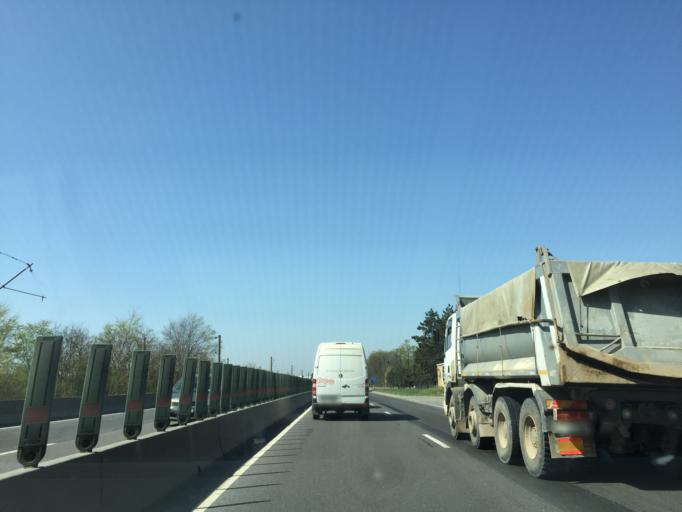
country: RO
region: Ilfov
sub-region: Comuna Otopeni
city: Otopeni
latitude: 44.5394
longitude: 26.1049
